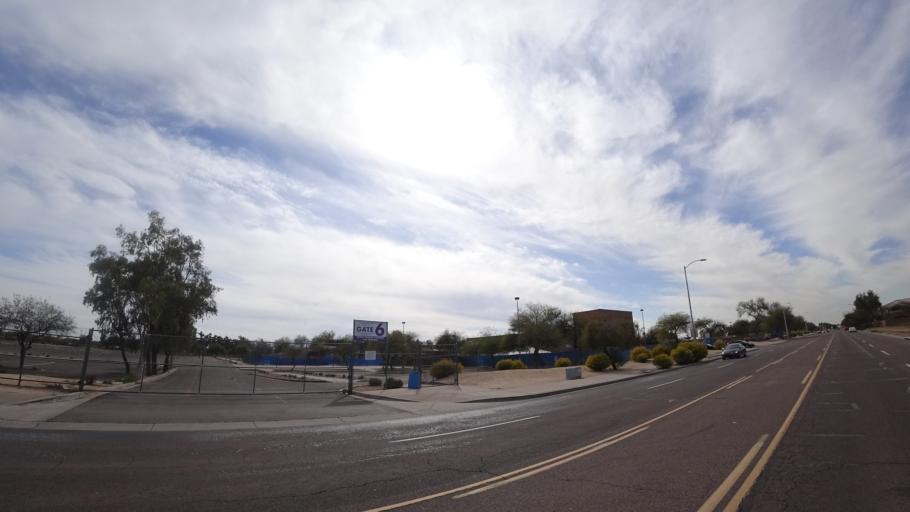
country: US
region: Arizona
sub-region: Maricopa County
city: Tolleson
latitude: 33.4727
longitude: -112.2310
